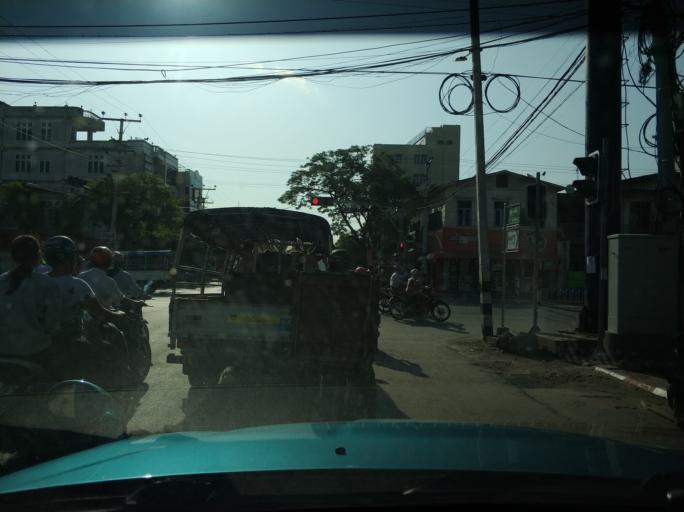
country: MM
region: Mandalay
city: Mandalay
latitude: 21.9660
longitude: 96.0859
